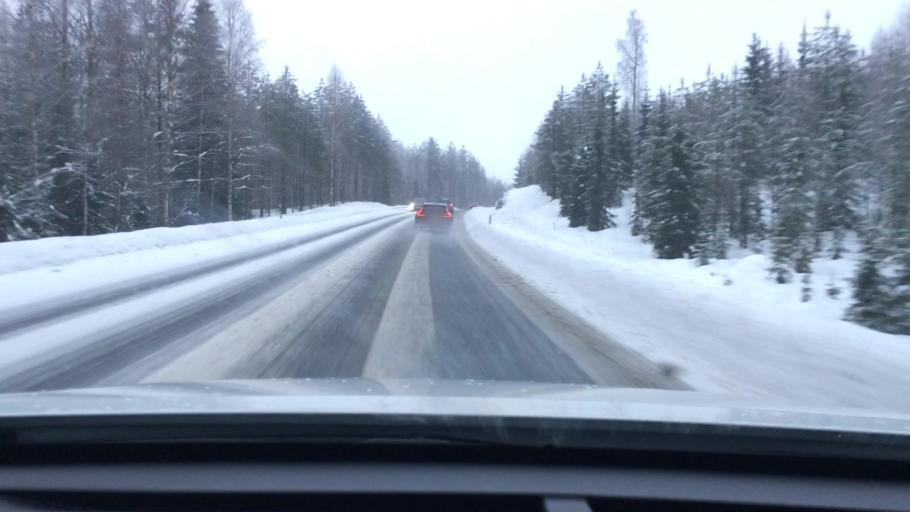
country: FI
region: Northern Savo
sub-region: Ylae-Savo
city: Sonkajaervi
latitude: 63.7680
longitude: 27.4137
